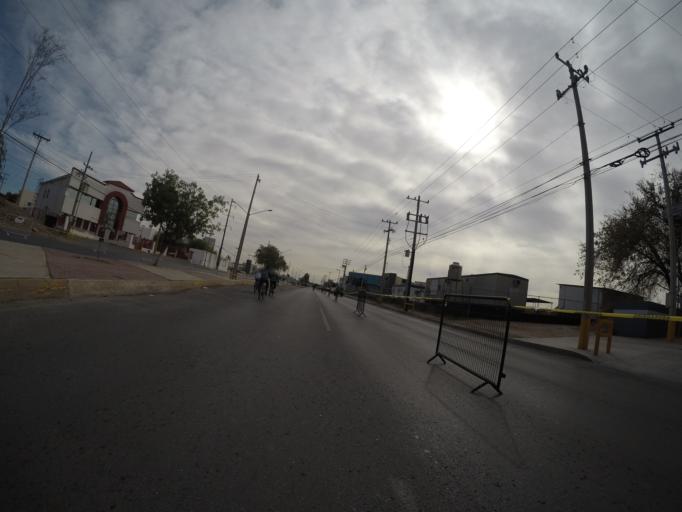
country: MX
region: Chihuahua
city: Ciudad Juarez
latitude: 31.7258
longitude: -106.4037
